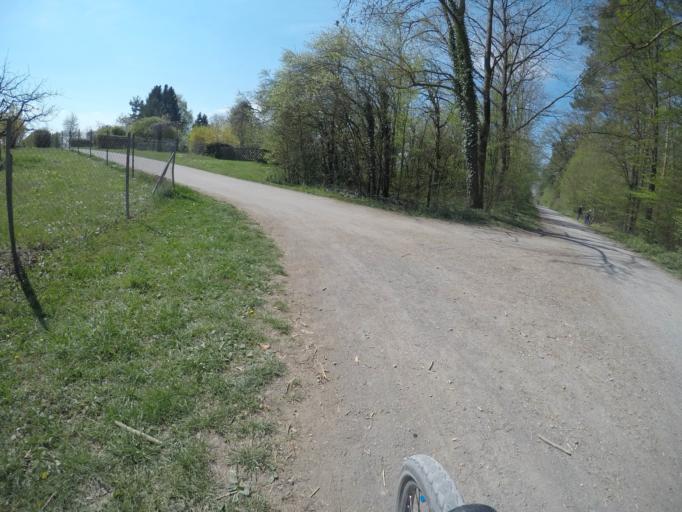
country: DE
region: Baden-Wuerttemberg
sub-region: Regierungsbezirk Stuttgart
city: Rutesheim
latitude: 48.8218
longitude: 8.9423
